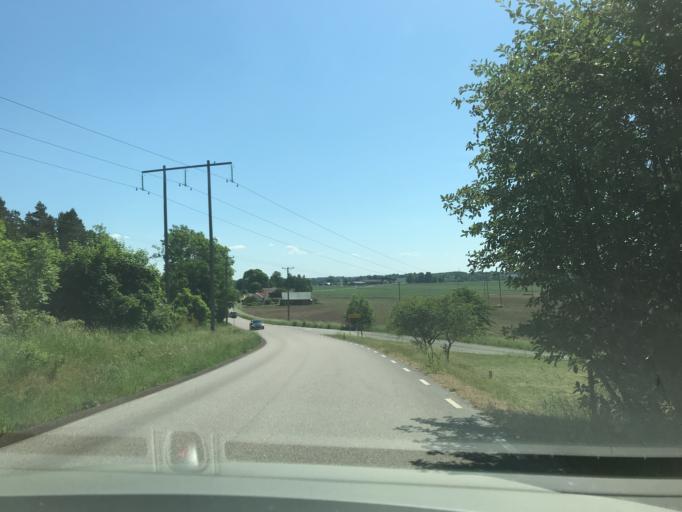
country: SE
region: Vaestra Goetaland
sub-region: Gotene Kommun
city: Kallby
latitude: 58.5260
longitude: 13.3210
